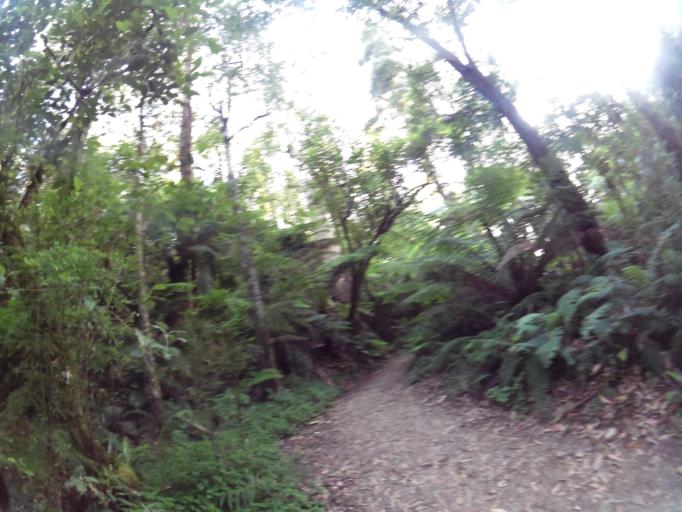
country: AU
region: Victoria
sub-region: Colac-Otway
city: Apollo Bay
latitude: -38.5516
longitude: 143.7515
